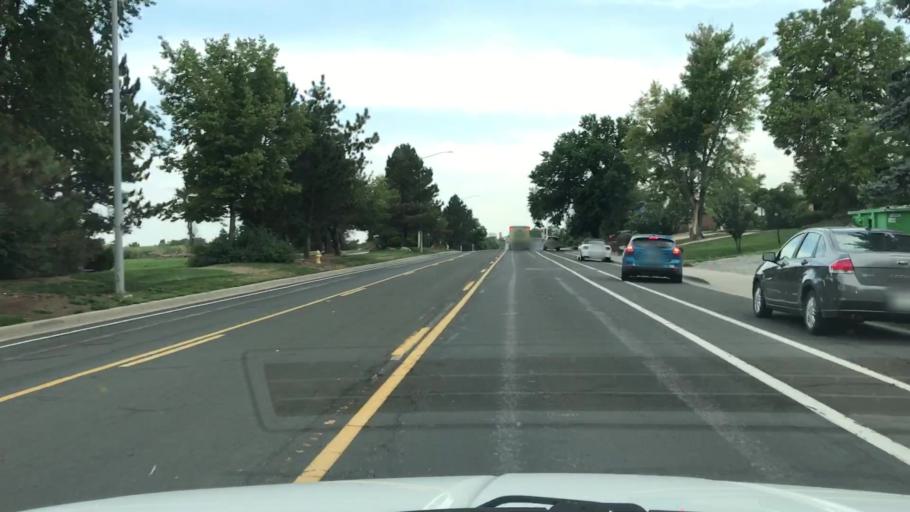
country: US
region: Colorado
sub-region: Broomfield County
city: Broomfield
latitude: 39.9273
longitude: -105.0718
